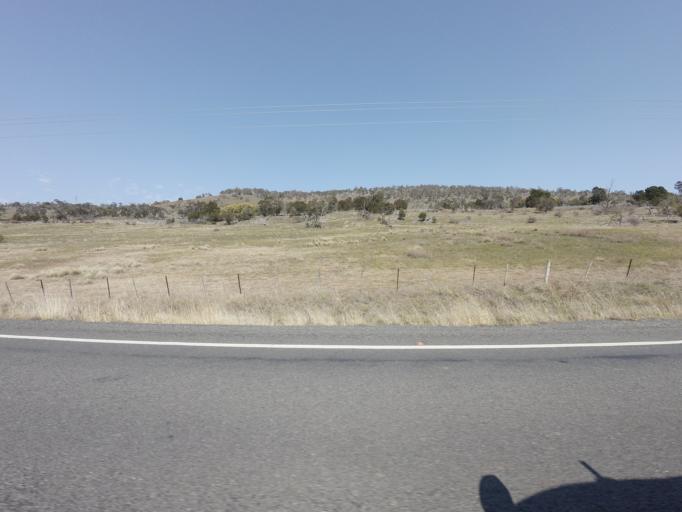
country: AU
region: Tasmania
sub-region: Northern Midlands
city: Evandale
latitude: -41.8158
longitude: 147.5677
